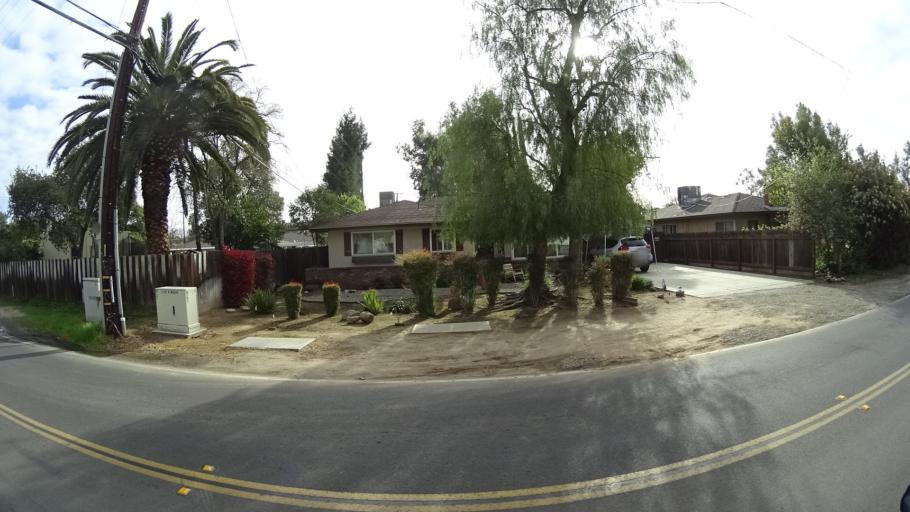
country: US
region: California
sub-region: Fresno County
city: Fresno
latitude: 36.7936
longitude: -119.7996
